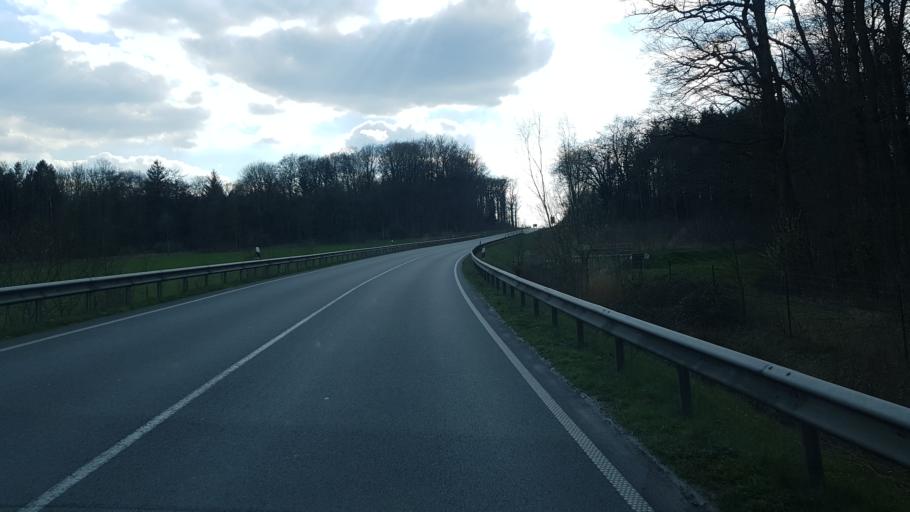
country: DE
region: Lower Saxony
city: Rastede
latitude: 53.2323
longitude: 8.2726
